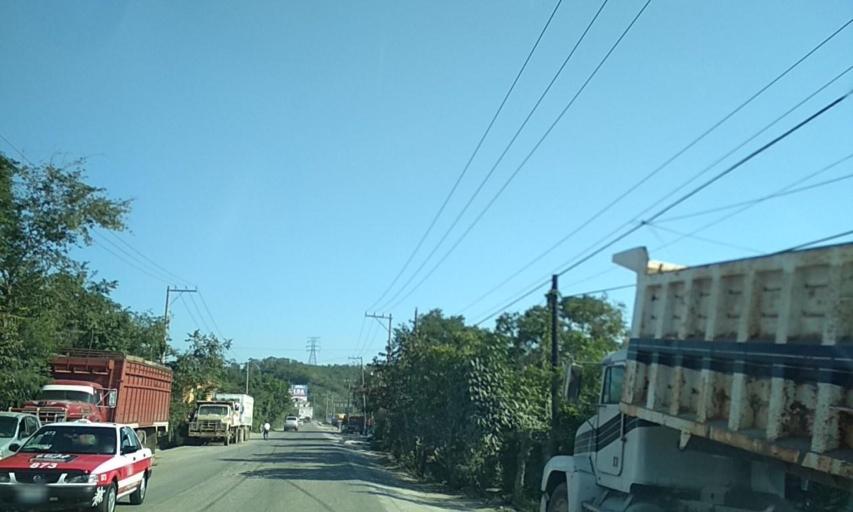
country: MX
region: Veracruz
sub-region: Papantla
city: El Chote
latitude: 20.4048
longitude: -97.3428
